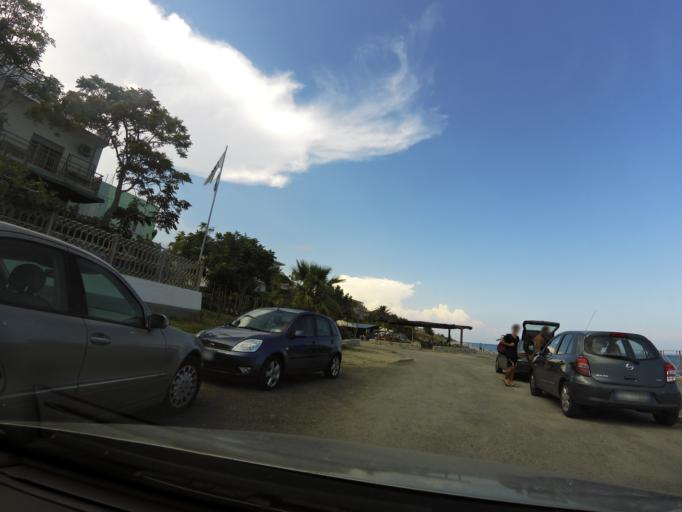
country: IT
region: Calabria
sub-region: Provincia di Reggio Calabria
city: Monasterace Marina
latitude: 38.4424
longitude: 16.5782
